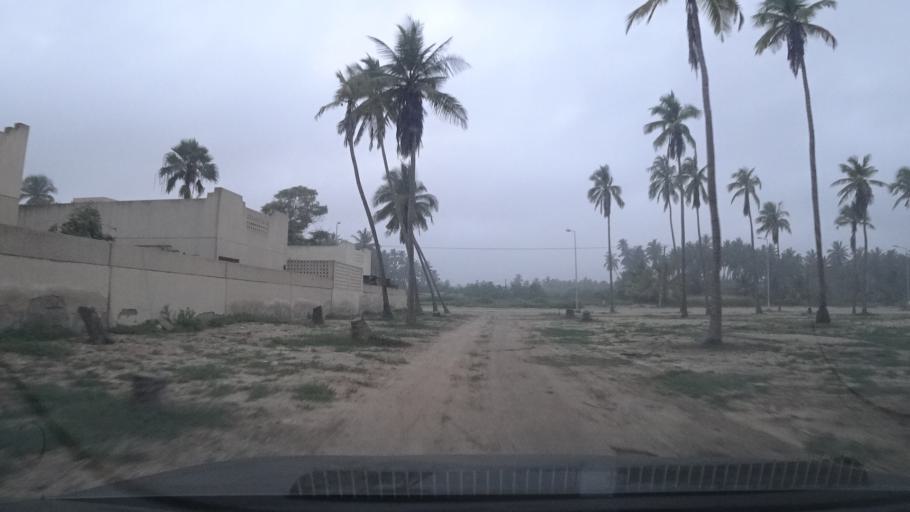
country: OM
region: Zufar
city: Salalah
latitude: 17.0036
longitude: 54.1188
